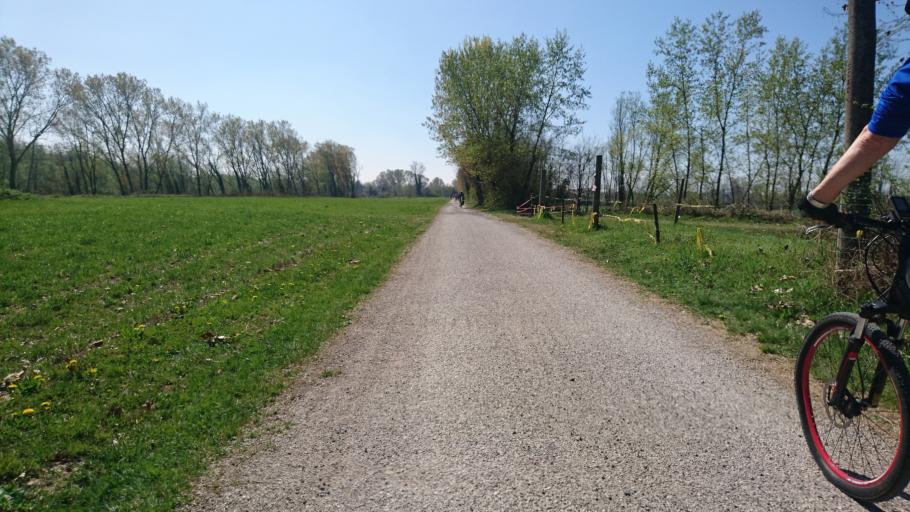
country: IT
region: Veneto
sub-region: Provincia di Padova
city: Grantorto
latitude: 45.5846
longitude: 11.7572
